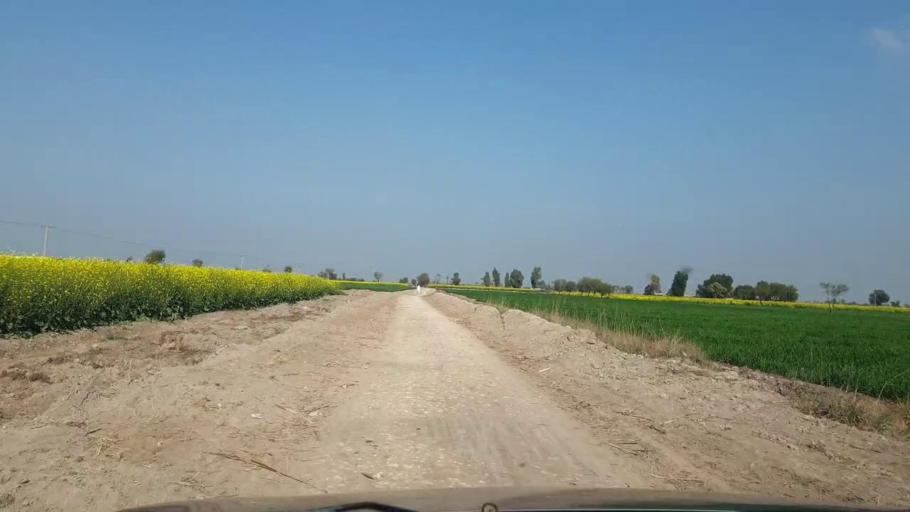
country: PK
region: Sindh
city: Sinjhoro
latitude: 26.0515
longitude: 68.7295
